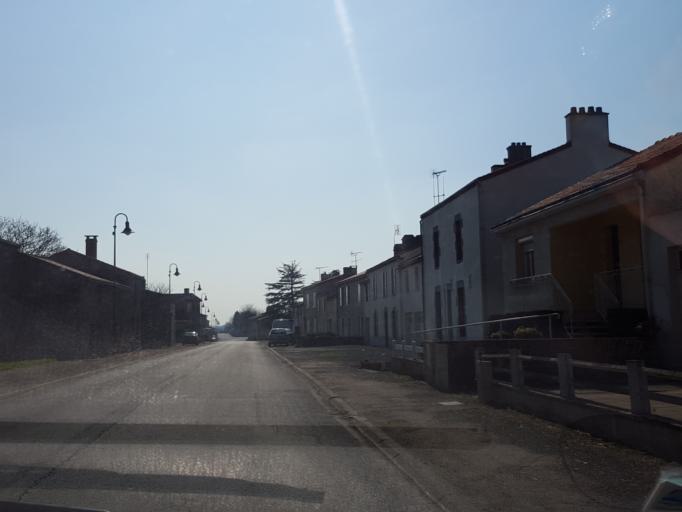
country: FR
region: Pays de la Loire
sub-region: Departement de la Vendee
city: Chauche
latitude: 46.8590
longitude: -1.2626
